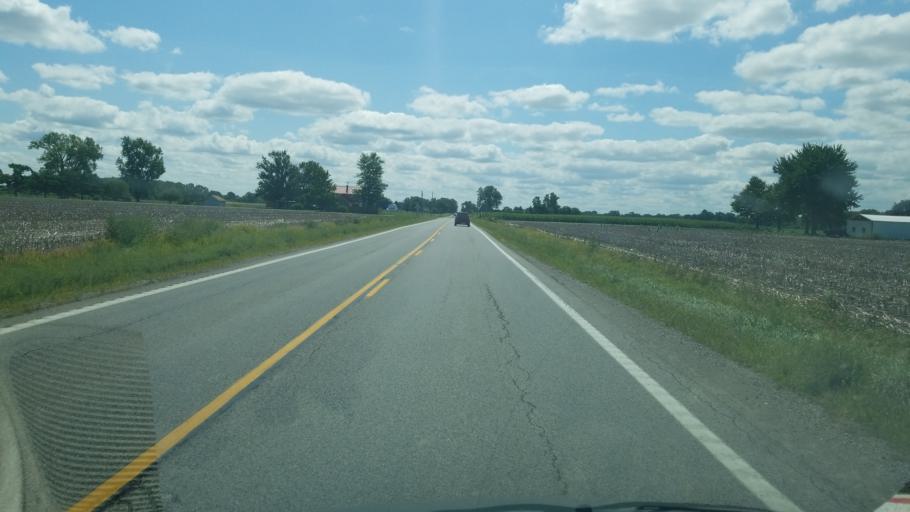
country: US
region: Ohio
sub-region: Fulton County
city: Delta
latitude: 41.6205
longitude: -84.0371
